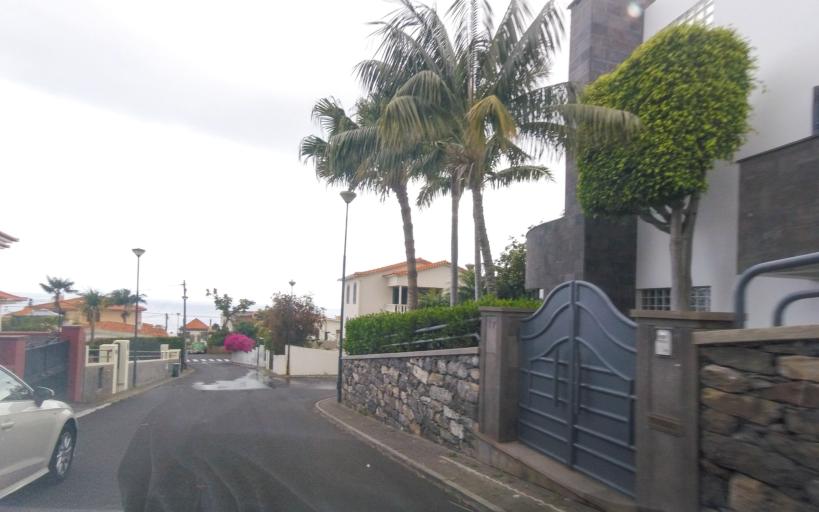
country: PT
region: Madeira
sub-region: Funchal
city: Nossa Senhora do Monte
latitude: 32.6553
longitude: -16.8977
